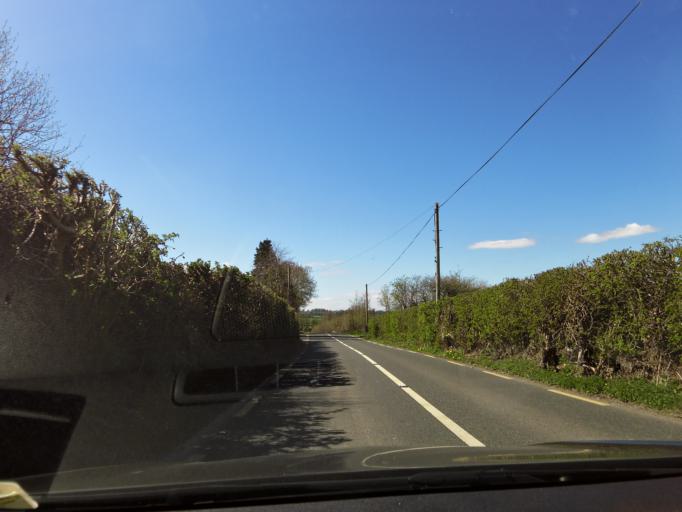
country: IE
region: Leinster
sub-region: Kildare
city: Moone
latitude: 53.0005
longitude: -6.8022
